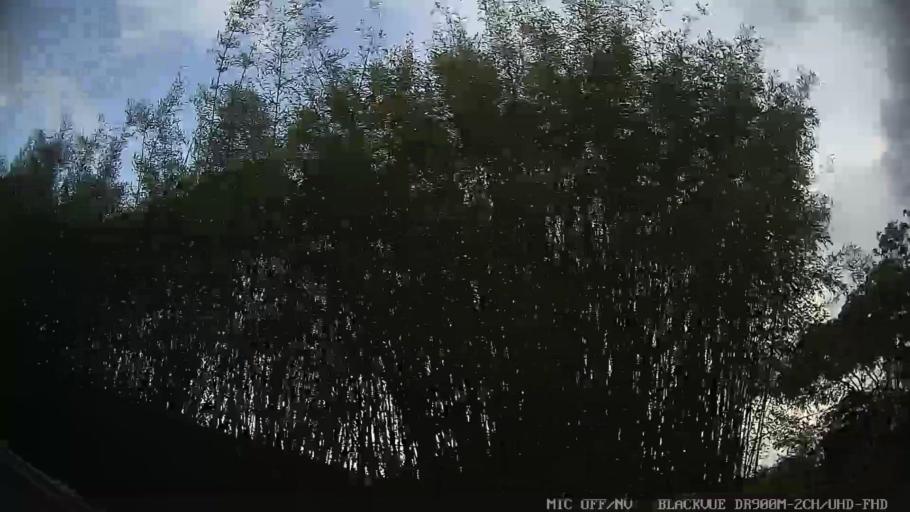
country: BR
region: Sao Paulo
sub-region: Itatiba
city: Itatiba
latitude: -22.9567
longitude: -46.8209
